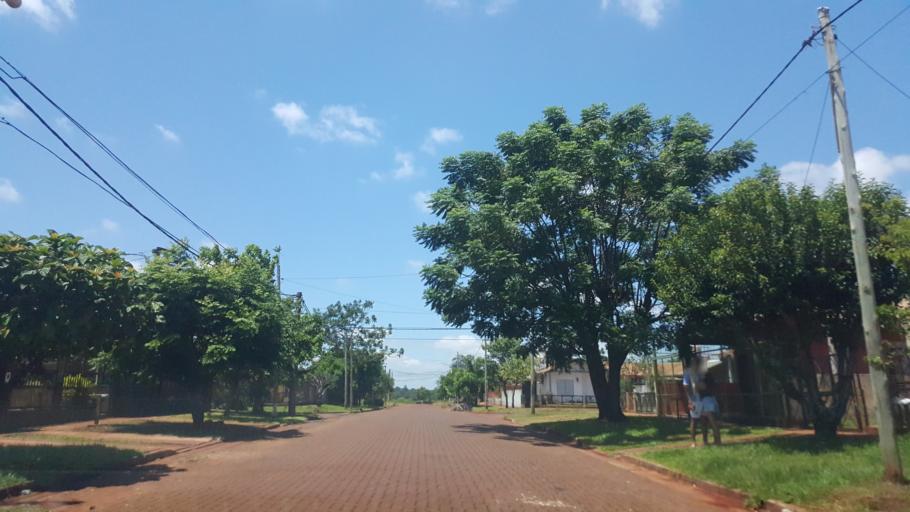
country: AR
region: Misiones
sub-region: Departamento de Capital
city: Posadas
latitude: -27.4184
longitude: -55.9511
